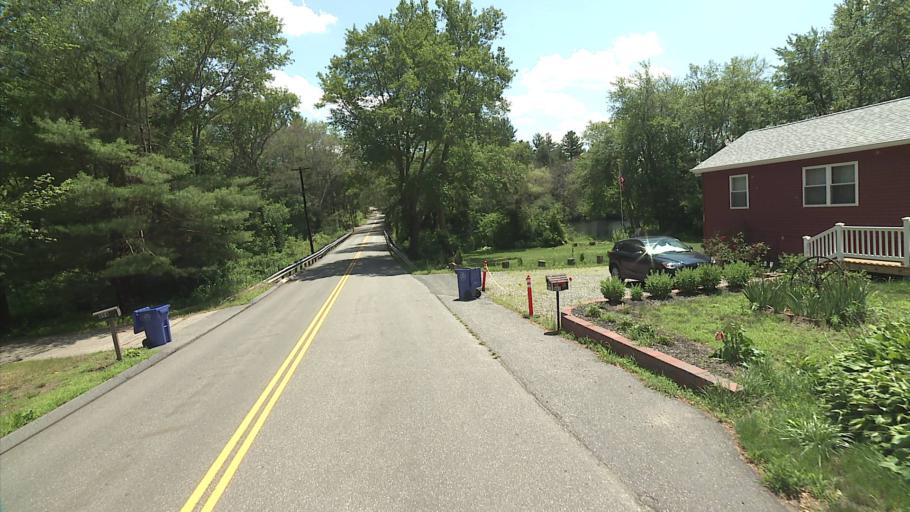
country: US
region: Connecticut
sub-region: New London County
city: Jewett City
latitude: 41.6094
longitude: -71.9287
